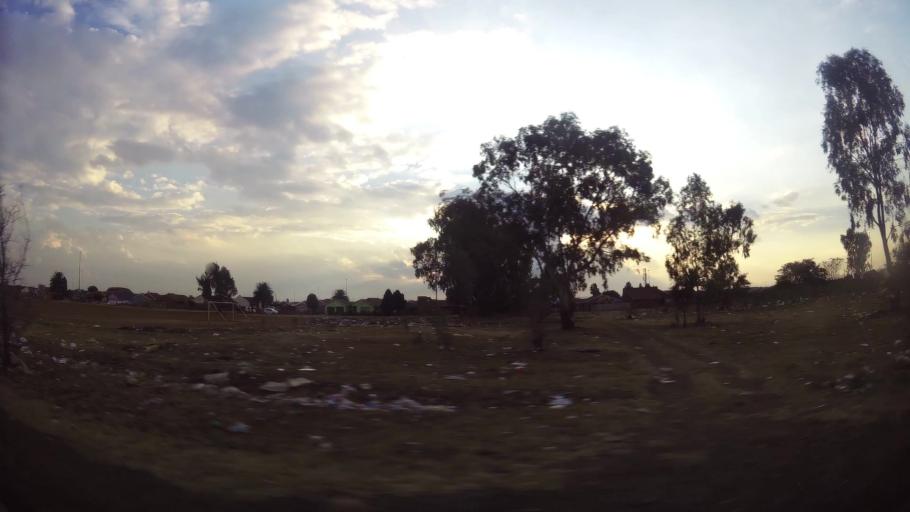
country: ZA
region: Gauteng
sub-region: City of Johannesburg Metropolitan Municipality
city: Orange Farm
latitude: -26.5745
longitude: 27.8584
